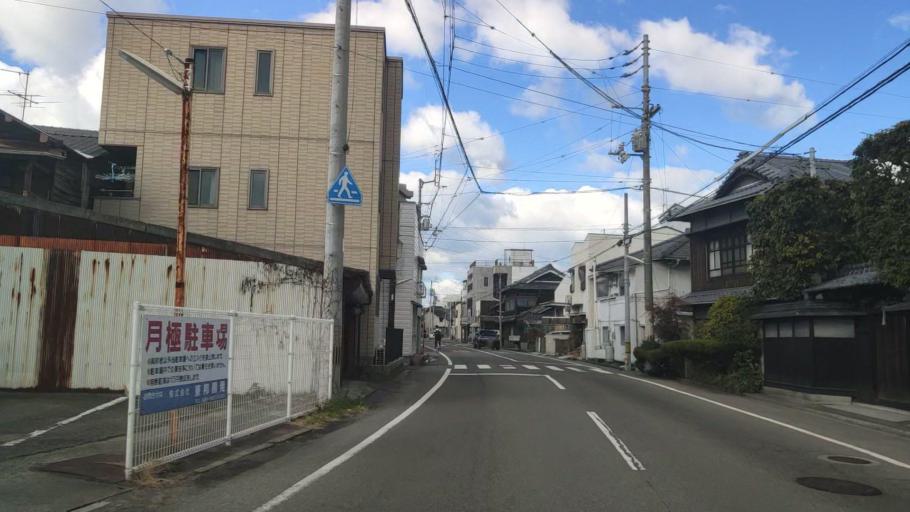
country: JP
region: Ehime
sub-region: Shikoku-chuo Shi
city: Matsuyama
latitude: 33.8645
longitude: 132.7156
